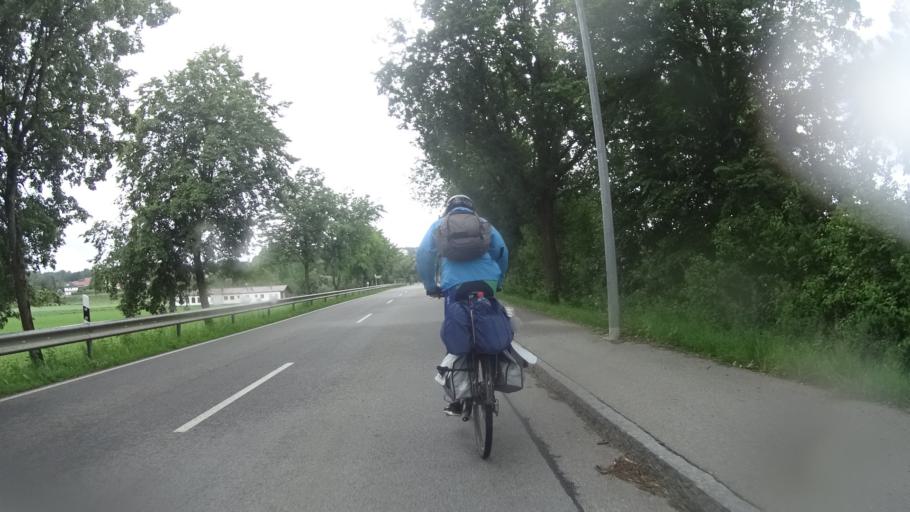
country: DE
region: Bavaria
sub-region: Lower Bavaria
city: Hebertsfelden
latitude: 48.4116
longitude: 12.8180
